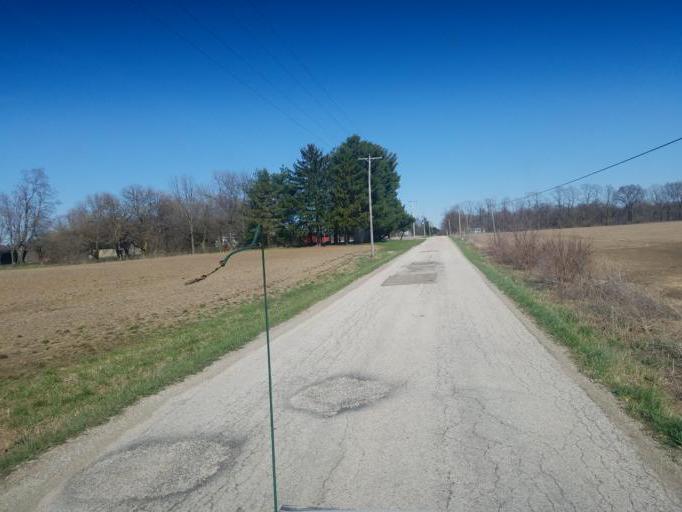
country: US
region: Ohio
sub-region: Morrow County
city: Mount Gilead
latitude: 40.5864
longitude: -82.8802
